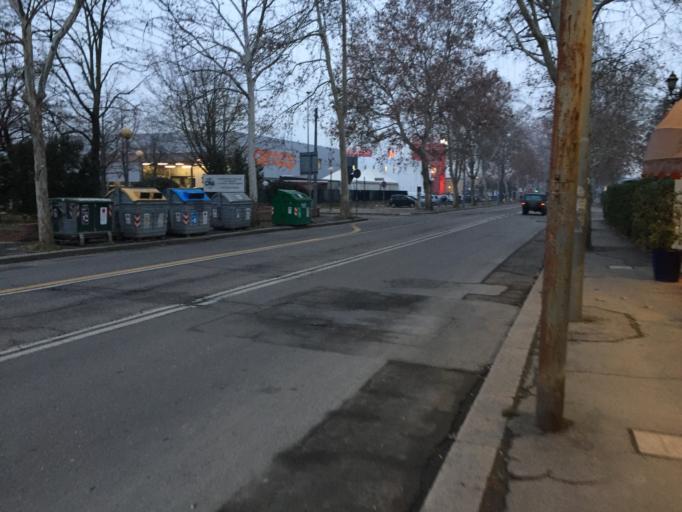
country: IT
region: Emilia-Romagna
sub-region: Provincia di Bologna
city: Calderara di Reno
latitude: 44.5203
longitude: 11.2669
